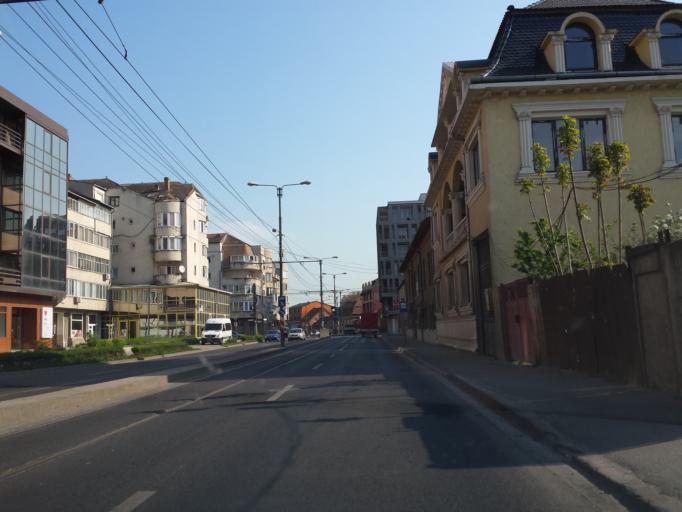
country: RO
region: Timis
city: Timisoara
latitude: 45.7614
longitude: 21.2600
